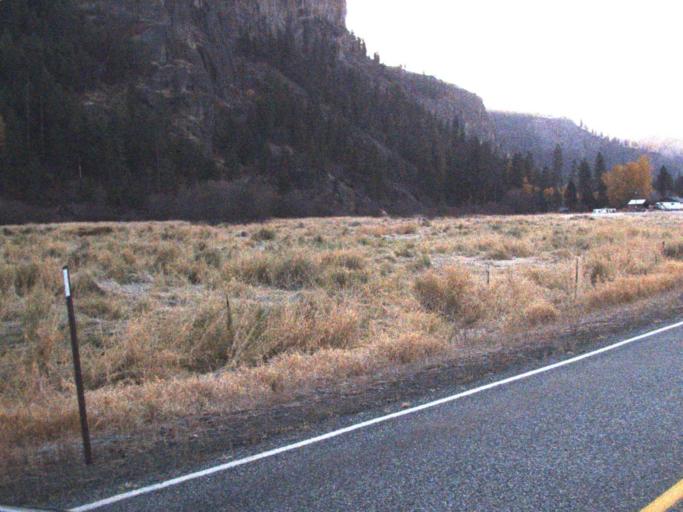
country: US
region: Washington
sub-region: Ferry County
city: Republic
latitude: 48.4645
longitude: -118.7534
